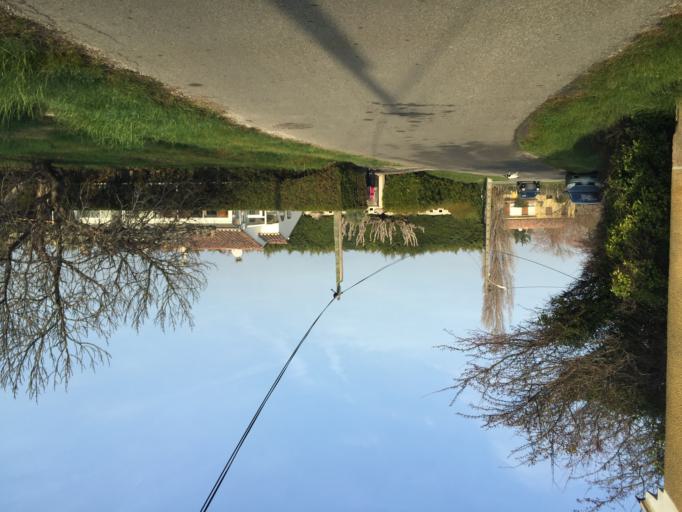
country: FR
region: Provence-Alpes-Cote d'Azur
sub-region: Departement du Vaucluse
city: Jonquieres
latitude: 44.1230
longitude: 4.8957
